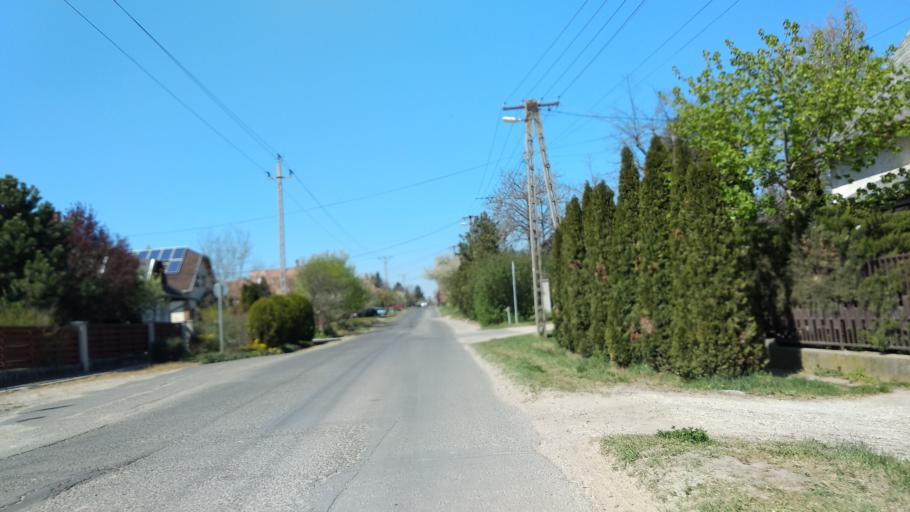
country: HU
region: Pest
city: Godollo
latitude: 47.5849
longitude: 19.3546
